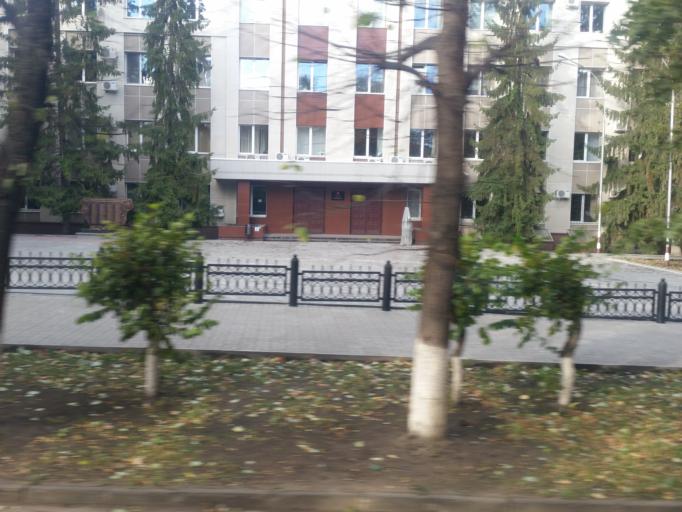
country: RU
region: Ulyanovsk
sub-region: Ulyanovskiy Rayon
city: Ulyanovsk
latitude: 54.3138
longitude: 48.3866
